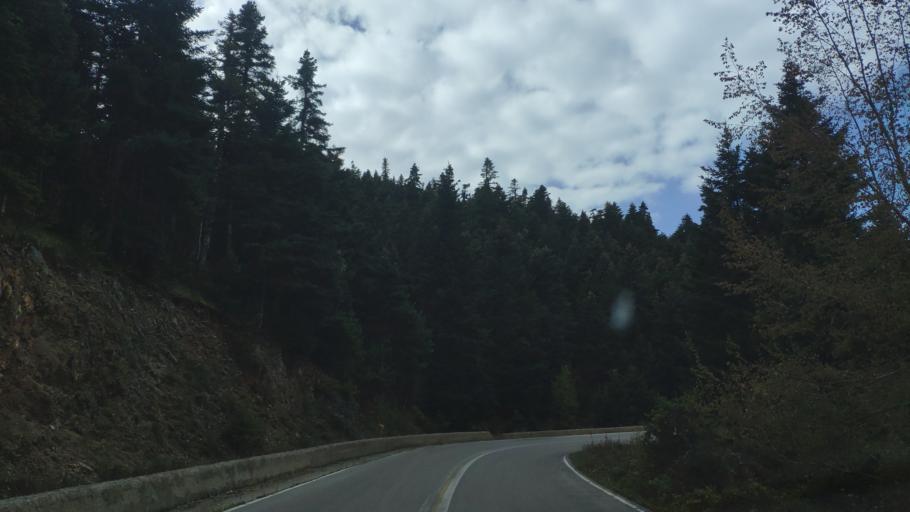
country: GR
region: Central Greece
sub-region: Nomos Fokidos
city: Amfissa
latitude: 38.6995
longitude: 22.3122
